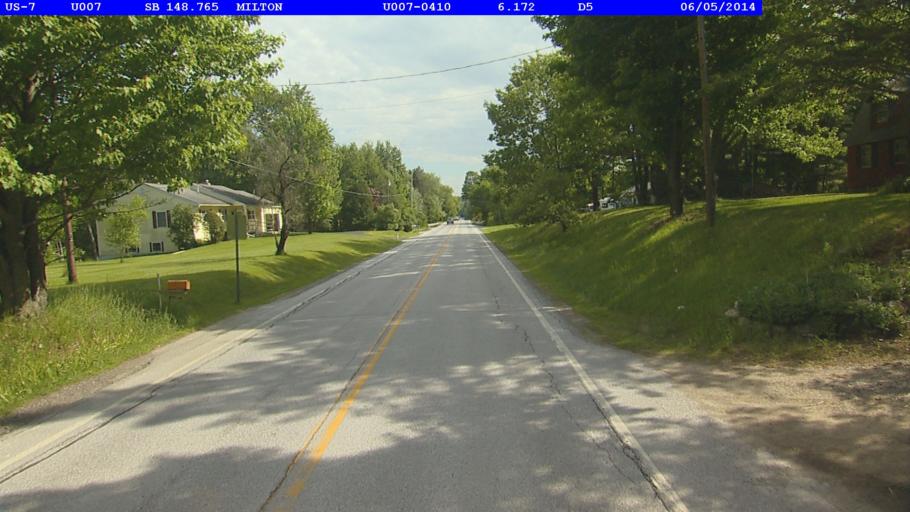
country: US
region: Vermont
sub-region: Chittenden County
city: Milton
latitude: 44.6555
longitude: -73.1138
